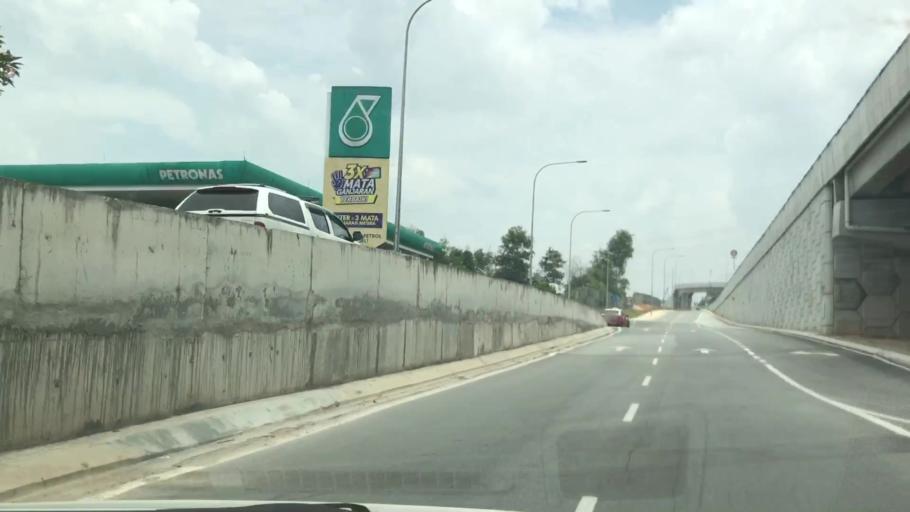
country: MY
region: Selangor
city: Kampong Baharu Balakong
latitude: 3.0494
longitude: 101.6804
